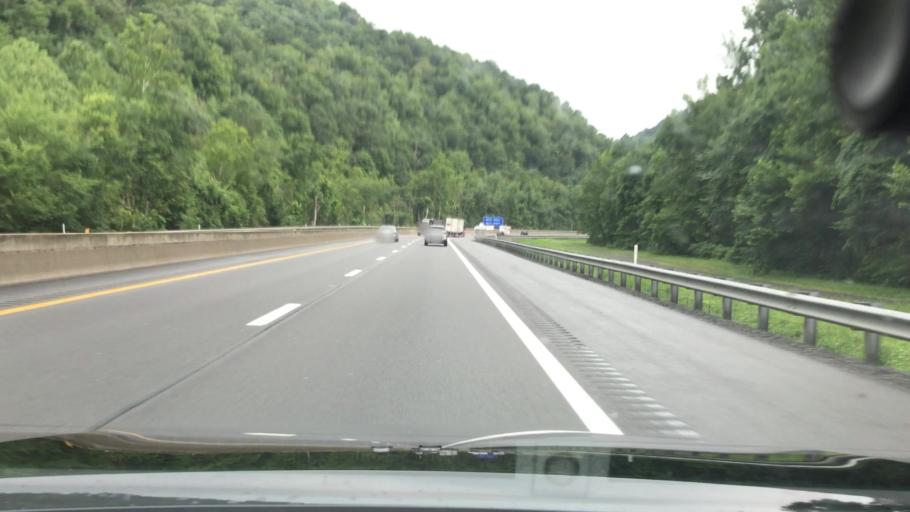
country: US
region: West Virginia
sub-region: Kanawha County
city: Montgomery
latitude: 38.0763
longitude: -81.3807
